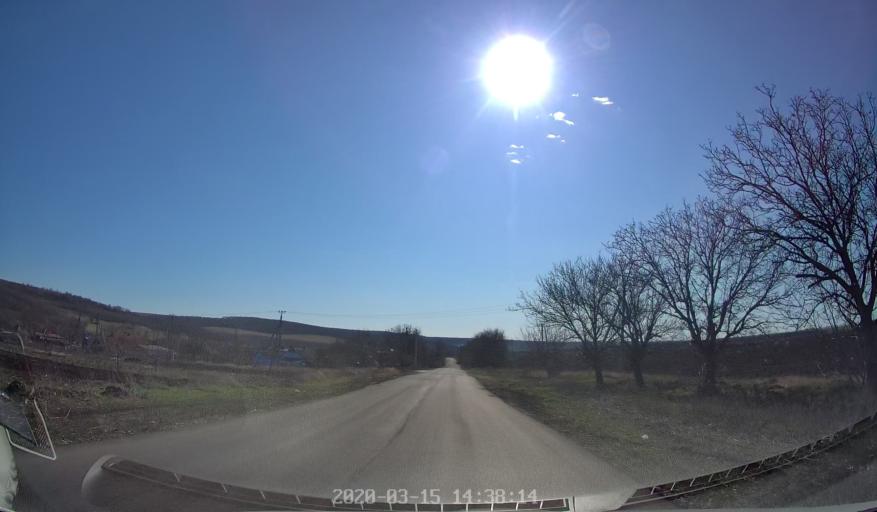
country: MD
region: Orhei
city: Orhei
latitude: 47.3076
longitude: 28.9193
